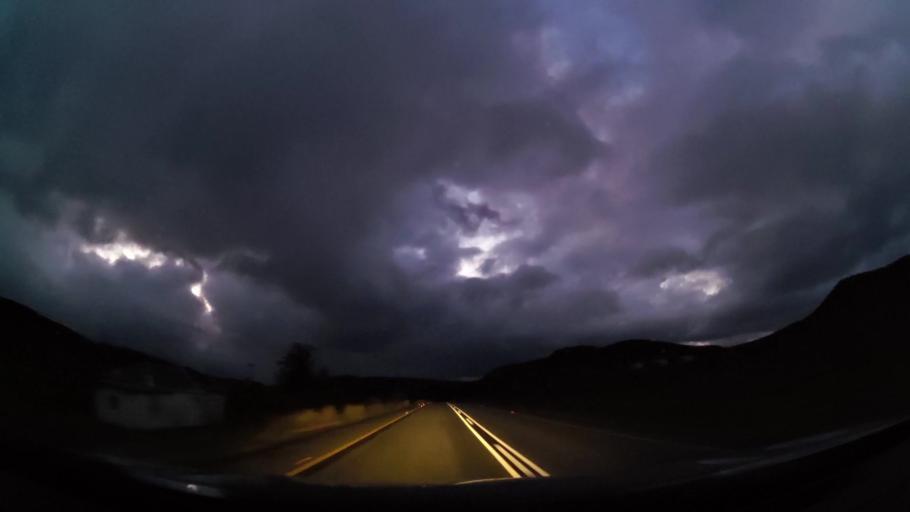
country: ZA
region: Western Cape
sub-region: Overberg District Municipality
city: Swellendam
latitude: -33.8990
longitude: 20.3876
